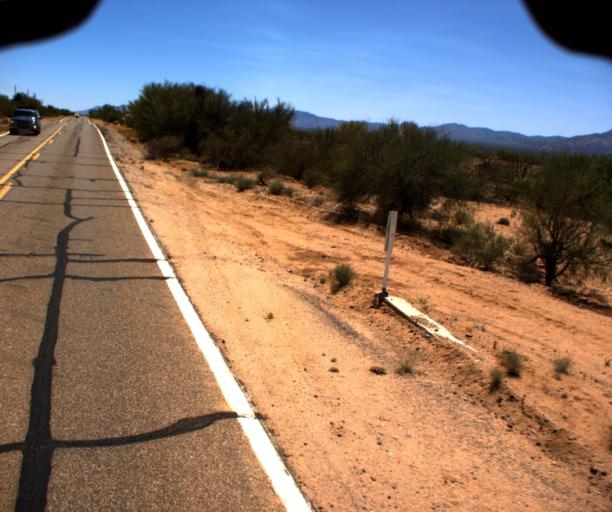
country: US
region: Arizona
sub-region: Pima County
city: Three Points
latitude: 32.0052
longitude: -111.3588
